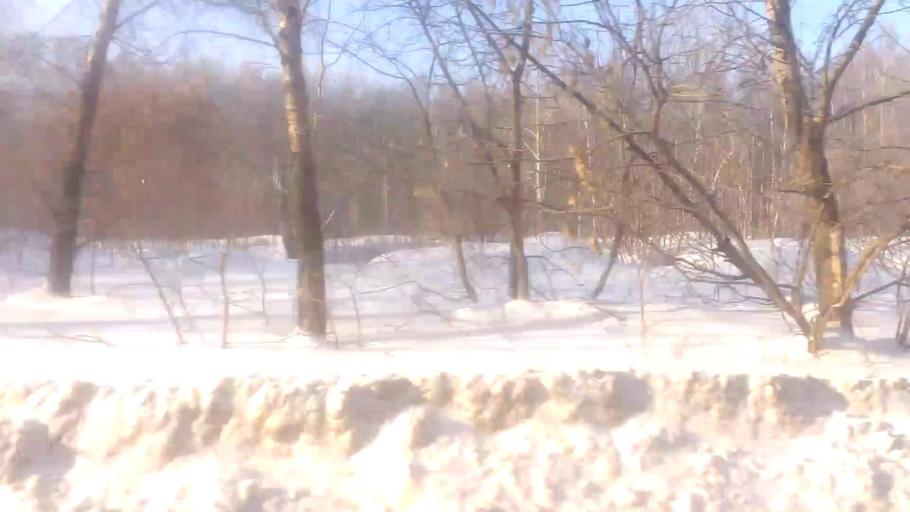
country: RU
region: Altai Krai
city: Novosilikatnyy
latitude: 53.3703
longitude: 83.6619
